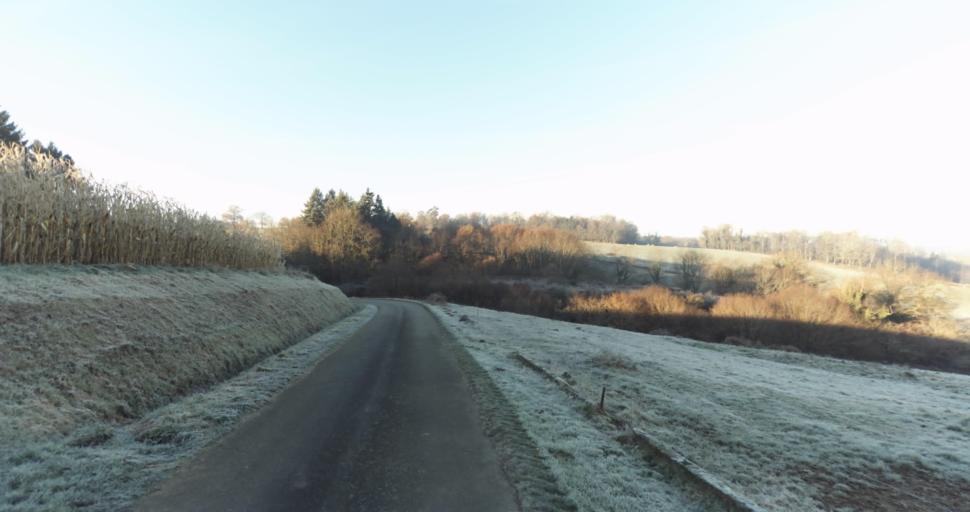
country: FR
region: Limousin
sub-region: Departement de la Haute-Vienne
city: Aixe-sur-Vienne
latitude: 45.8231
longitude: 1.1449
